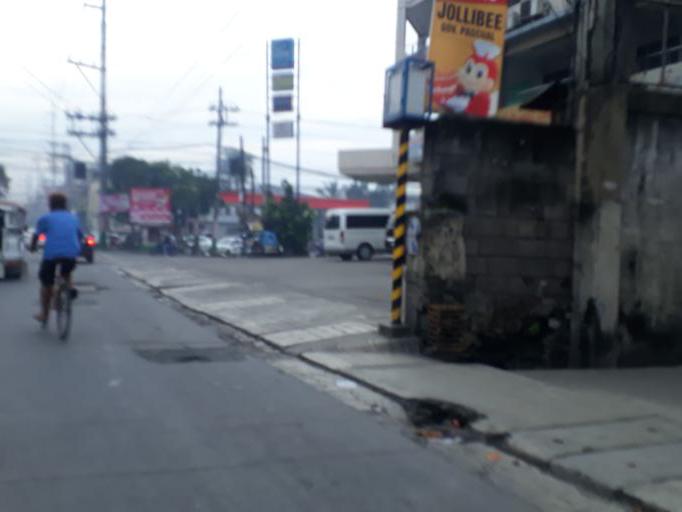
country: PH
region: Metro Manila
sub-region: Caloocan City
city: Niugan
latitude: 14.6686
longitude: 120.9656
